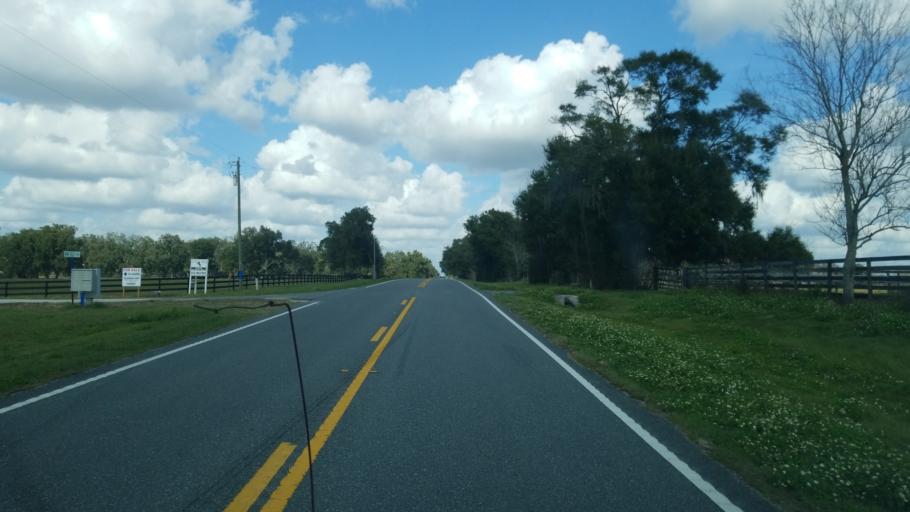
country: US
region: Florida
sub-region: Sumter County
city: Wildwood
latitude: 28.9050
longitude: -82.1200
